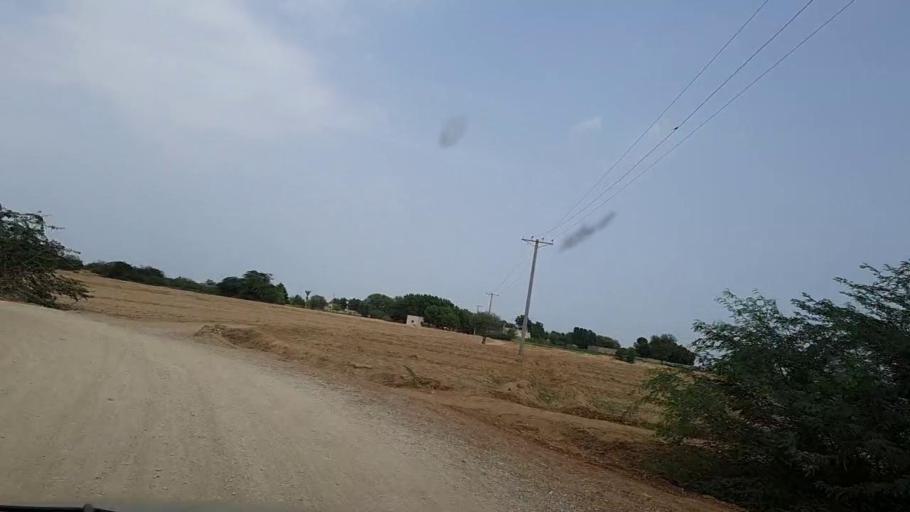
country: PK
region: Sindh
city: Kotri
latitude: 25.2767
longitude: 68.2555
